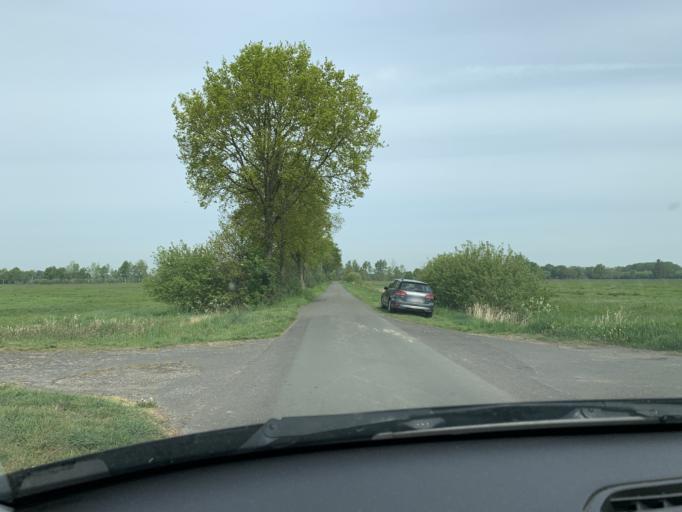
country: DE
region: Lower Saxony
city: Apen
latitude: 53.2392
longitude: 7.8308
